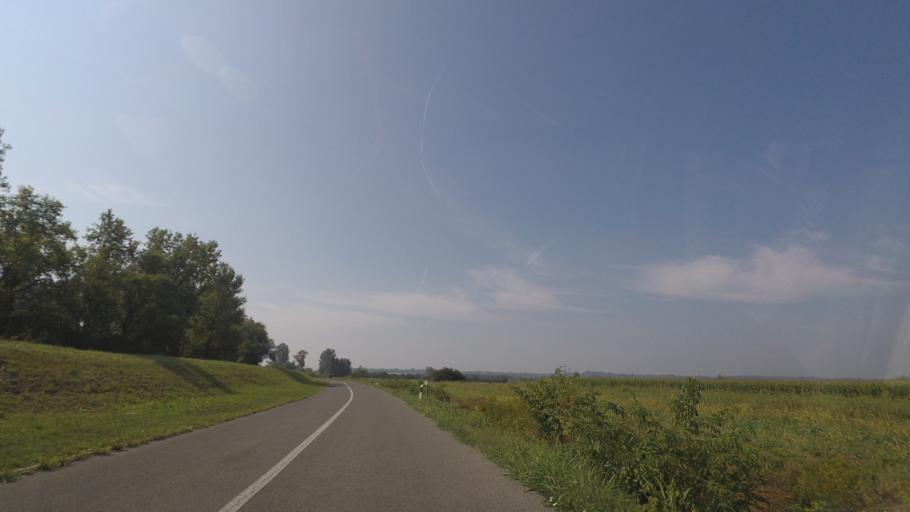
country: BA
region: Republika Srpska
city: Bosanska Dubica
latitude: 45.2183
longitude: 16.8327
